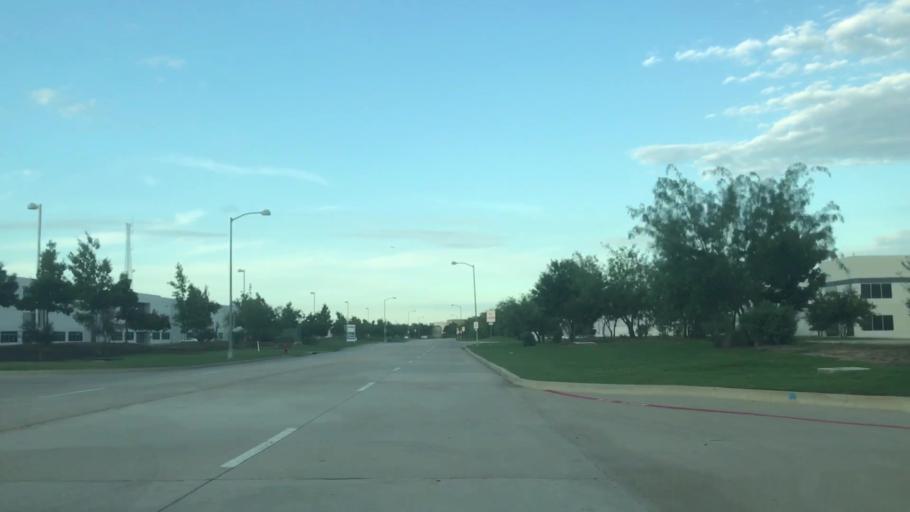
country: US
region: Texas
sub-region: Dallas County
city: Coppell
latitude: 32.9408
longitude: -97.0358
